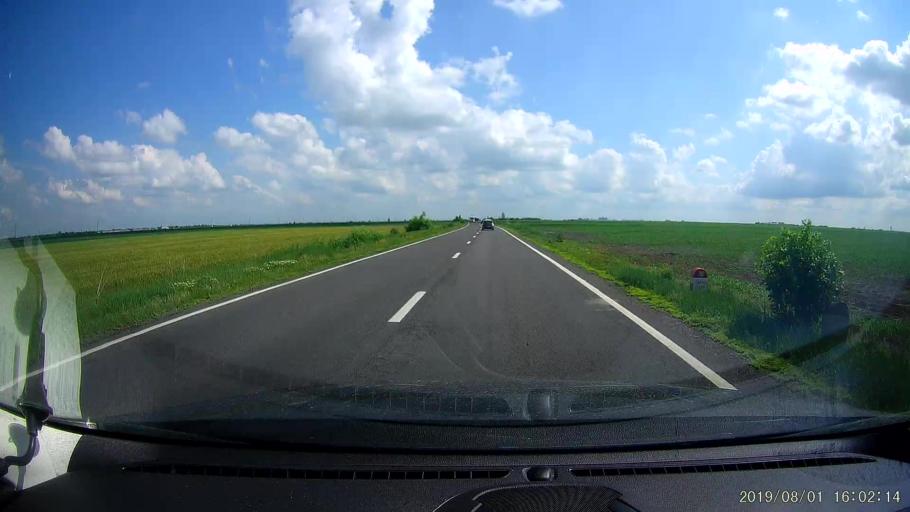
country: RO
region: Ialomita
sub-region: Comuna Ciulnita
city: Ciulnita
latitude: 44.4936
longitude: 27.3878
